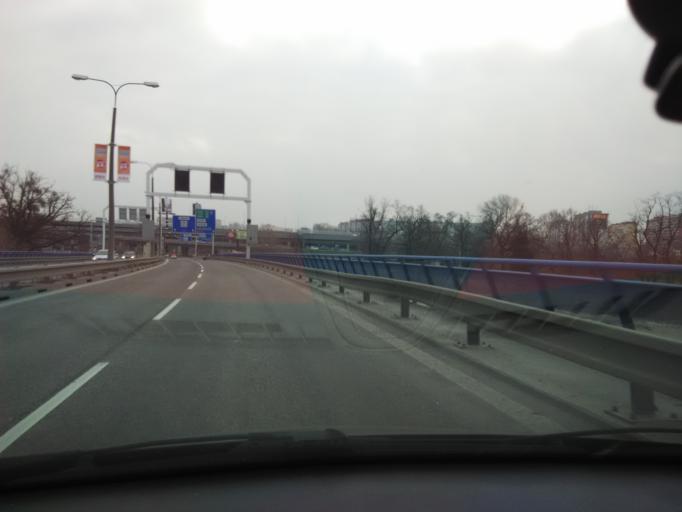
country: SK
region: Bratislavsky
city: Bratislava
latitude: 48.1343
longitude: 17.1281
